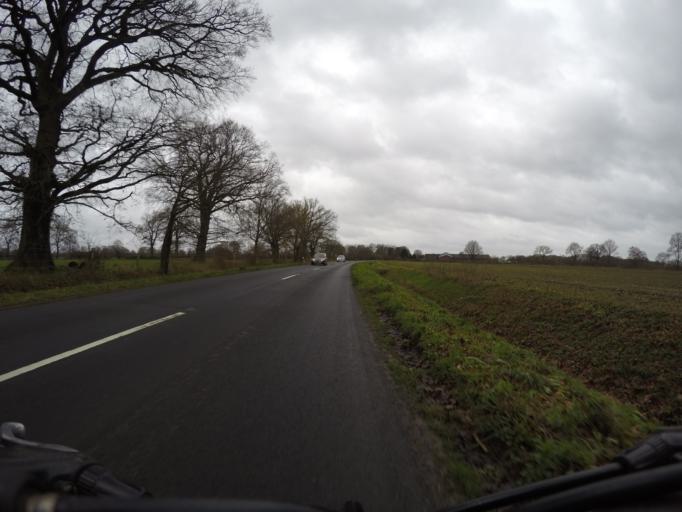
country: DE
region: Schleswig-Holstein
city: Quickborn
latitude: 53.7147
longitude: 9.8854
